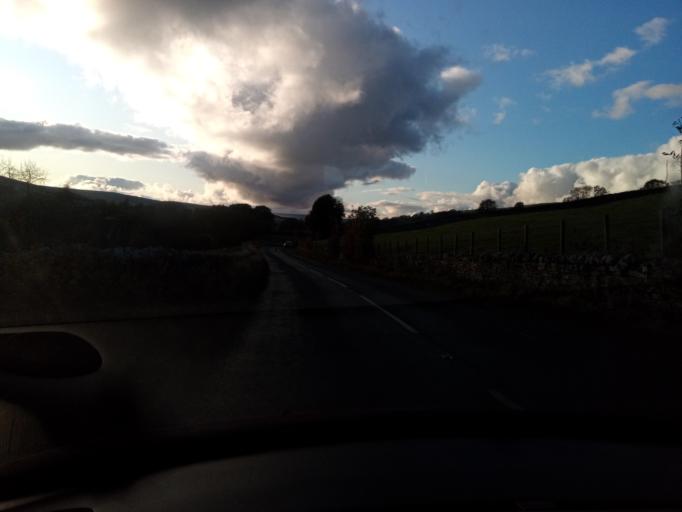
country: GB
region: England
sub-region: County Durham
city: Newbiggin
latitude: 54.7380
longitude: -2.1314
